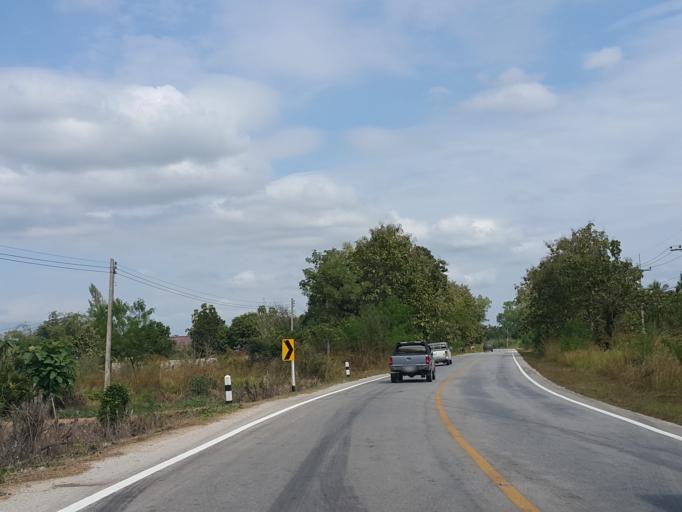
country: TH
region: Lampang
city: Lampang
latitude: 18.3705
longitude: 99.4559
